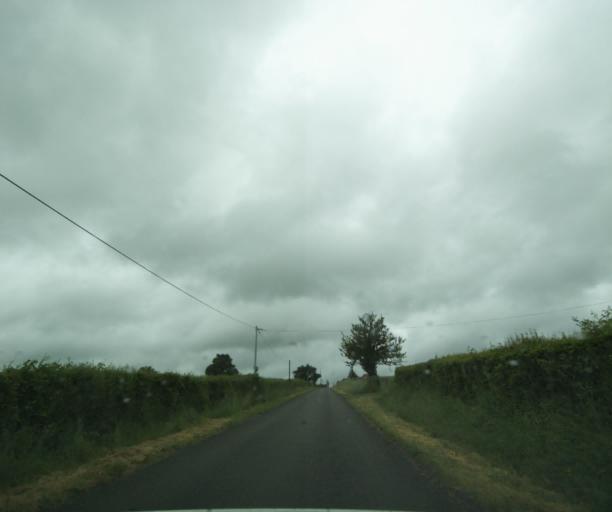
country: FR
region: Bourgogne
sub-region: Departement de Saone-et-Loire
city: Charolles
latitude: 46.4580
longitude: 4.4333
